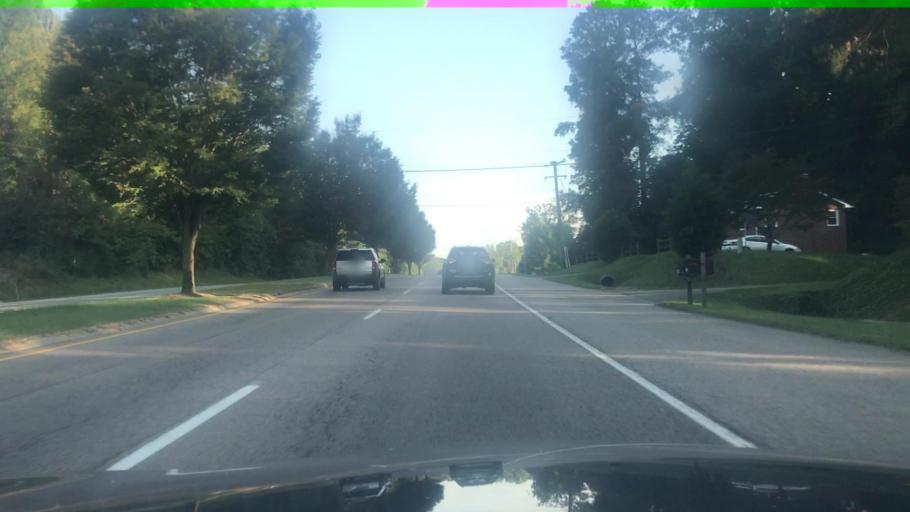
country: US
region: Virginia
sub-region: Chesterfield County
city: Brandermill
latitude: 37.4536
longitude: -77.5875
